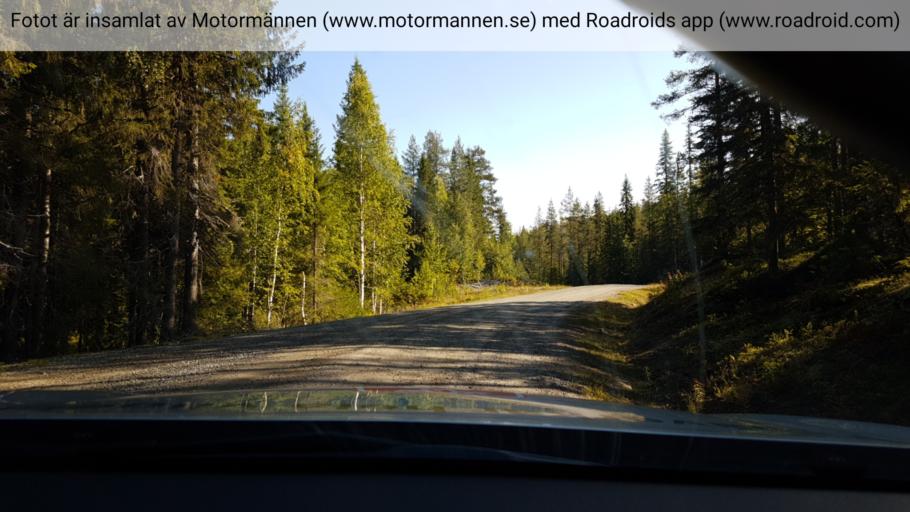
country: SE
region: Vaesterbotten
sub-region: Norsjo Kommun
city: Norsjoe
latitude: 64.7043
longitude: 19.5087
